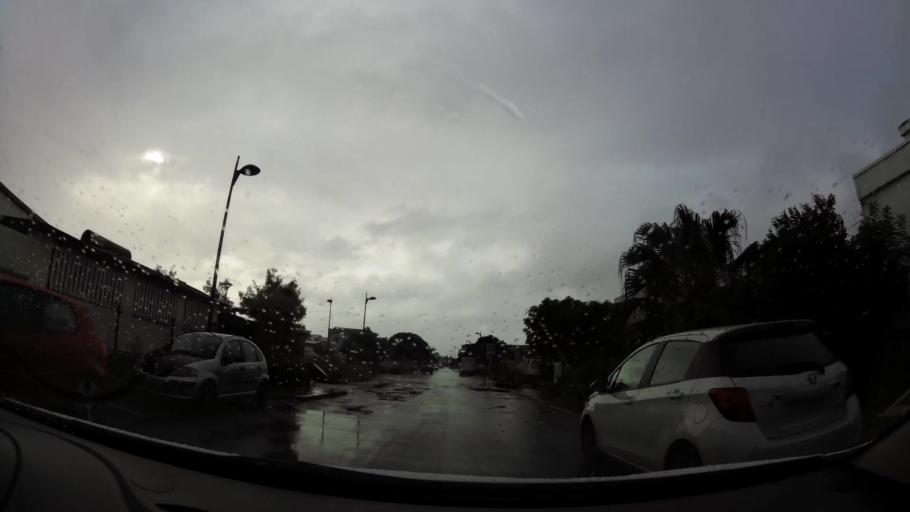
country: RE
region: Reunion
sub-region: Reunion
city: Saint-Andre
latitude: -20.9761
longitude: 55.6600
